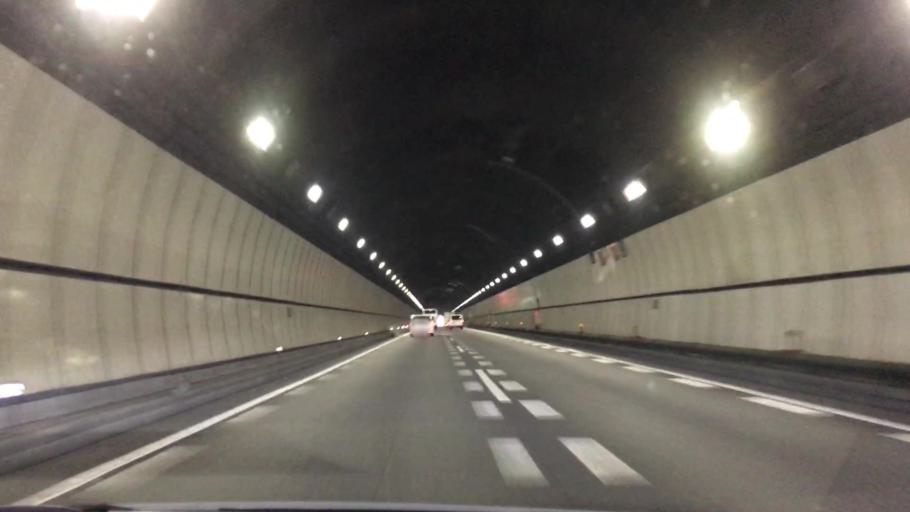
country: JP
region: Shizuoka
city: Shizuoka-shi
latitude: 35.0528
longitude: 138.5130
